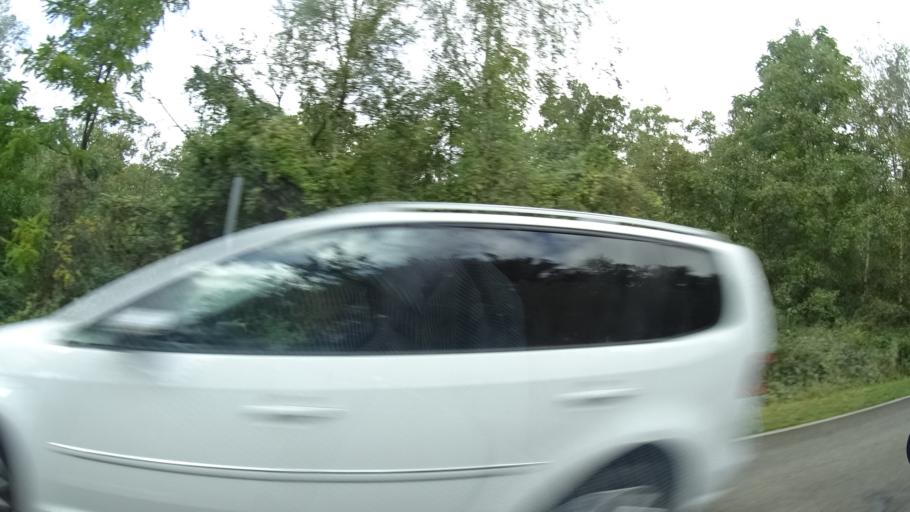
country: DE
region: Baden-Wuerttemberg
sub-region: Karlsruhe Region
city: Ostringen
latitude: 49.1953
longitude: 8.6866
